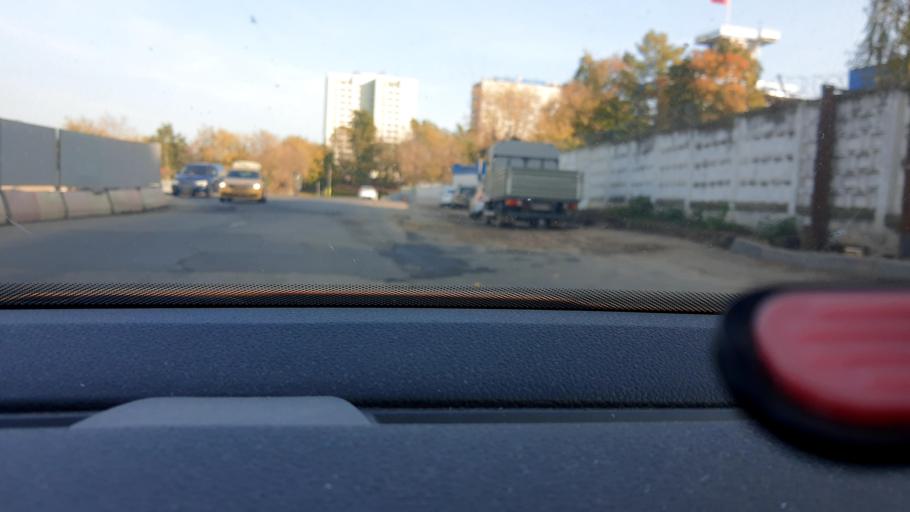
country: RU
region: Moscow
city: Novovladykino
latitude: 55.8504
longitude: 37.5815
